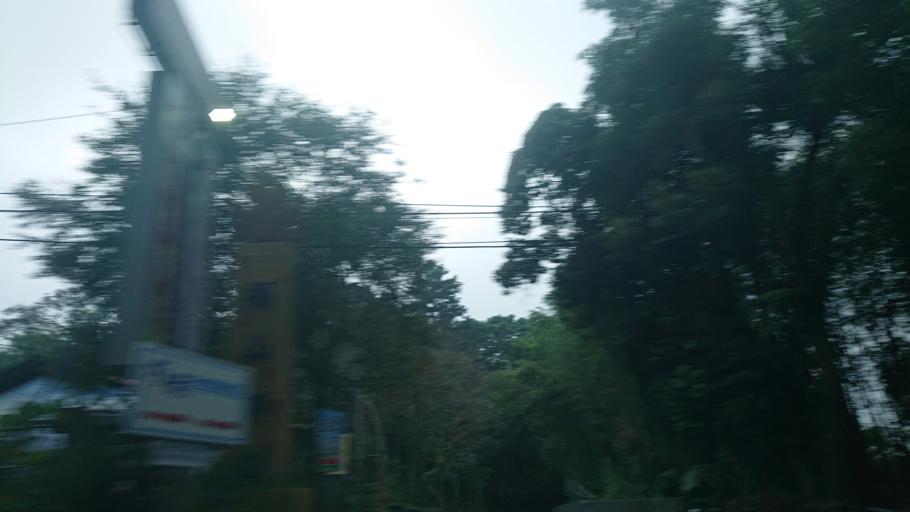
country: TW
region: Taiwan
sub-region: Chiayi
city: Jiayi Shi
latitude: 23.4611
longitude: 120.7222
